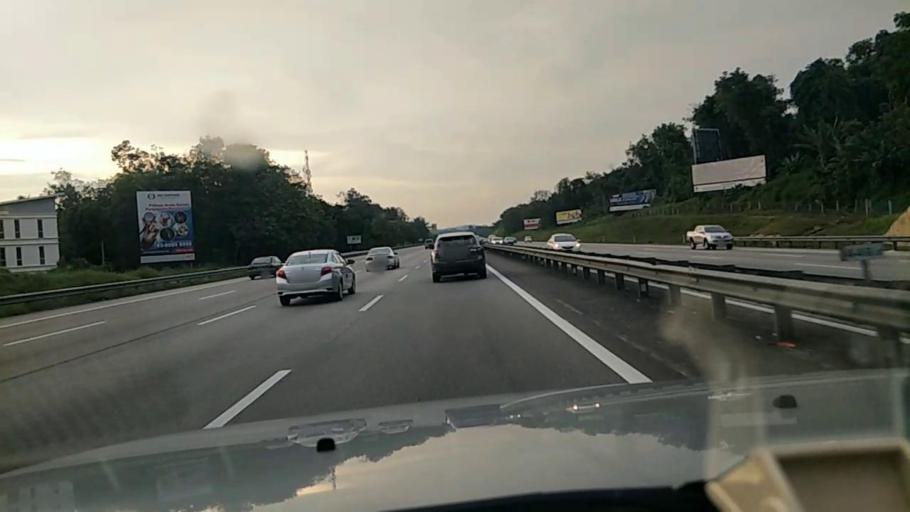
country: MY
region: Selangor
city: Kuang
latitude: 3.2536
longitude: 101.5608
